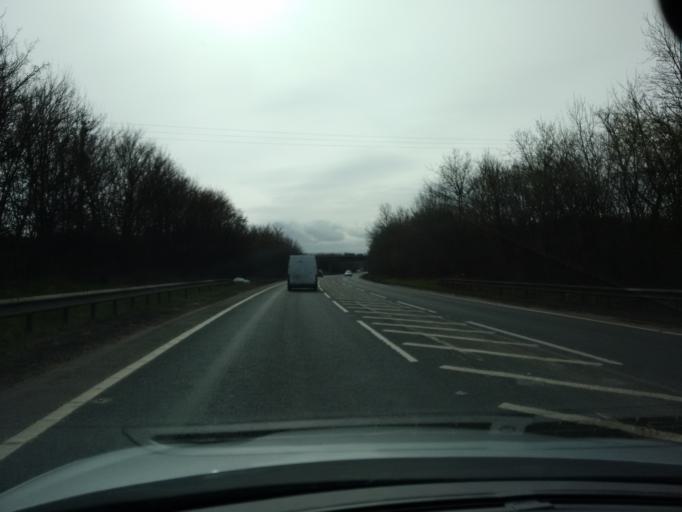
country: GB
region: England
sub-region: Worcestershire
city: Badsey
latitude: 52.1001
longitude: -1.9227
